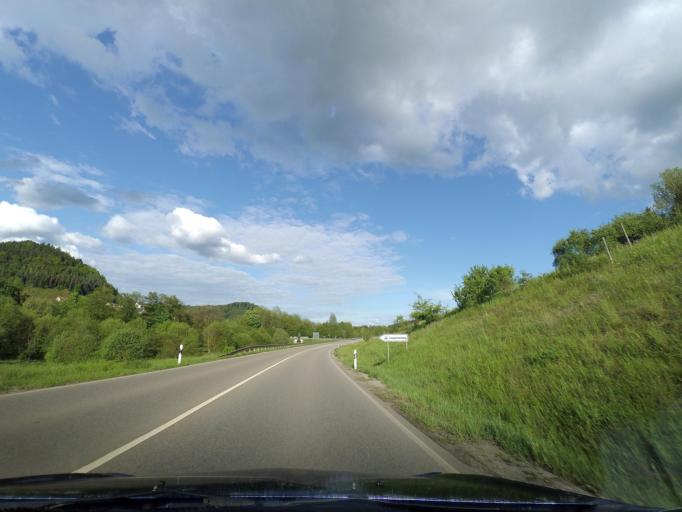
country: DE
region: Baden-Wuerttemberg
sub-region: Regierungsbezirk Stuttgart
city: Fichtenberg
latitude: 48.9863
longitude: 9.6959
